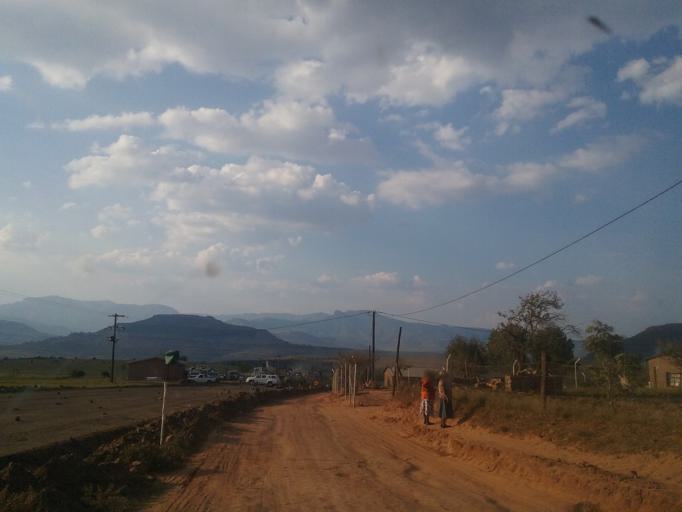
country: LS
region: Quthing
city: Quthing
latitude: -30.4161
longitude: 27.5984
